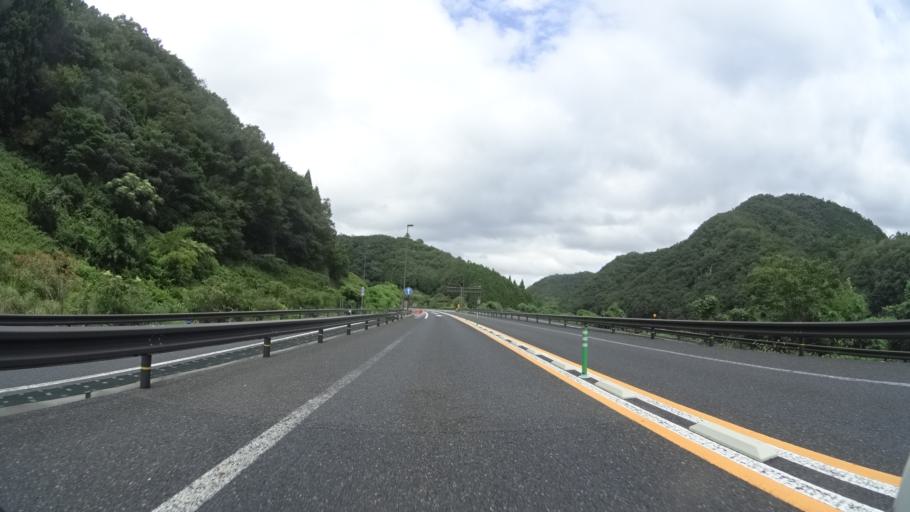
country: JP
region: Hyogo
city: Yamazakicho-nakabirose
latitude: 35.0611
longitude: 134.3640
